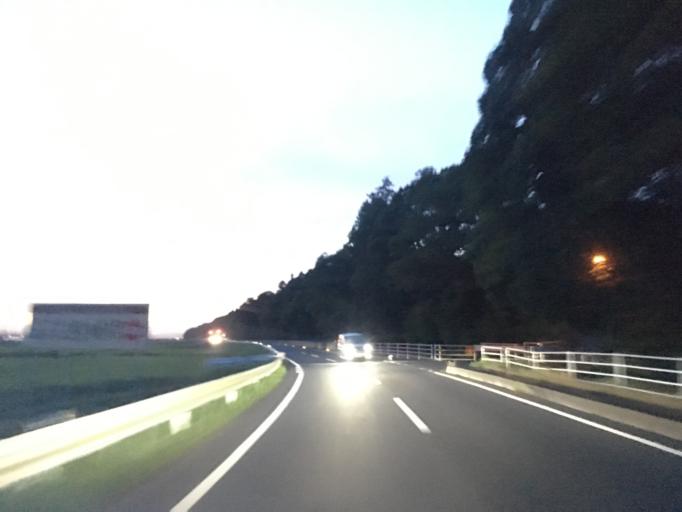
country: JP
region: Ibaraki
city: Katsuta
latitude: 36.3866
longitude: 140.5129
